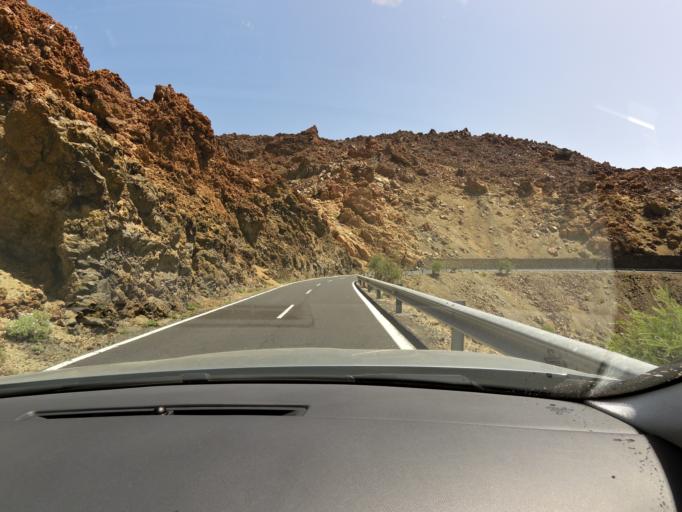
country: ES
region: Canary Islands
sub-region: Provincia de Santa Cruz de Tenerife
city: Los Realejos
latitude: 28.2608
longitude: -16.5969
